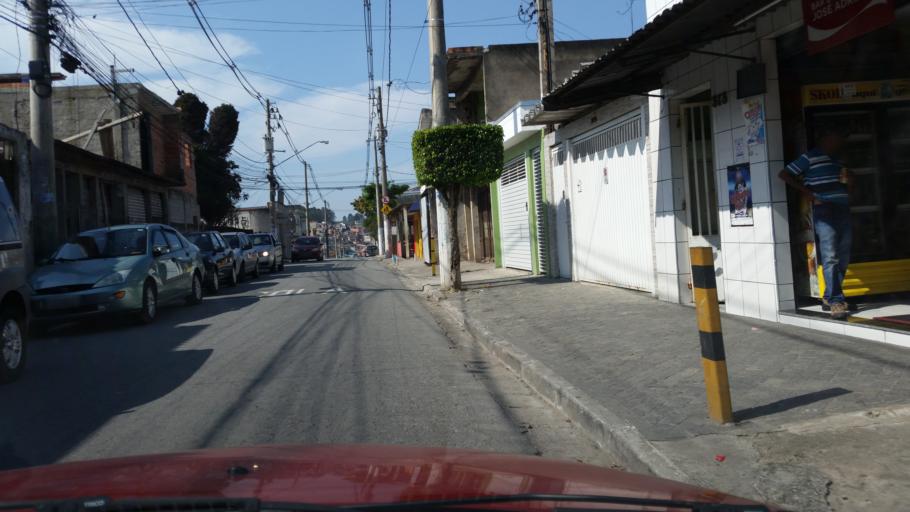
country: BR
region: Sao Paulo
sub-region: Ferraz De Vasconcelos
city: Ferraz de Vasconcelos
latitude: -23.5636
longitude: -46.4221
